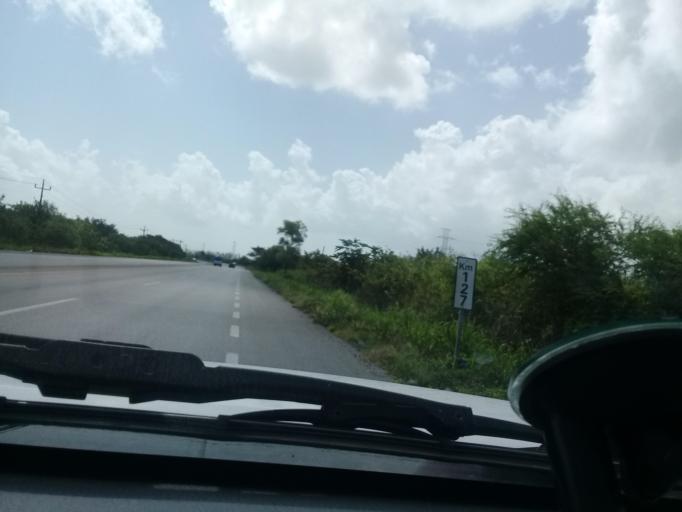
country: MX
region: Veracruz
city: Moralillo
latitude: 22.2123
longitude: -97.9667
